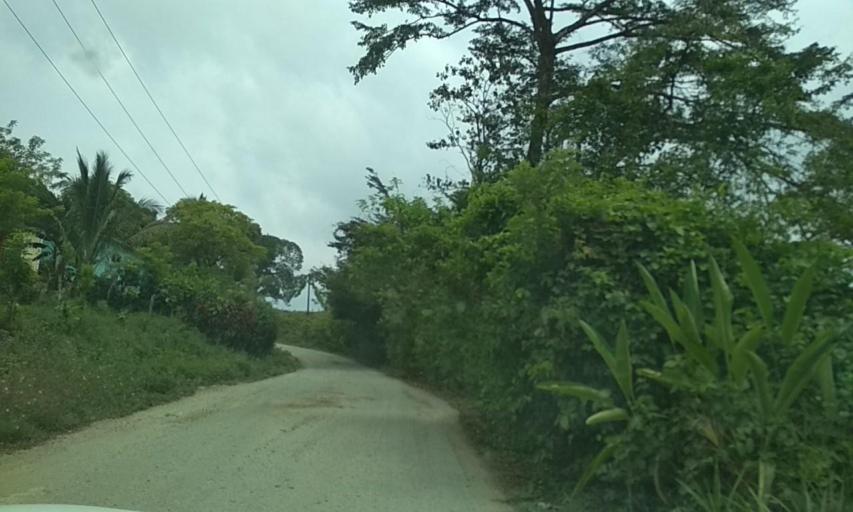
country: MX
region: Veracruz
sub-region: Uxpanapa
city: Poblado 10
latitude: 17.4969
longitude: -94.1399
